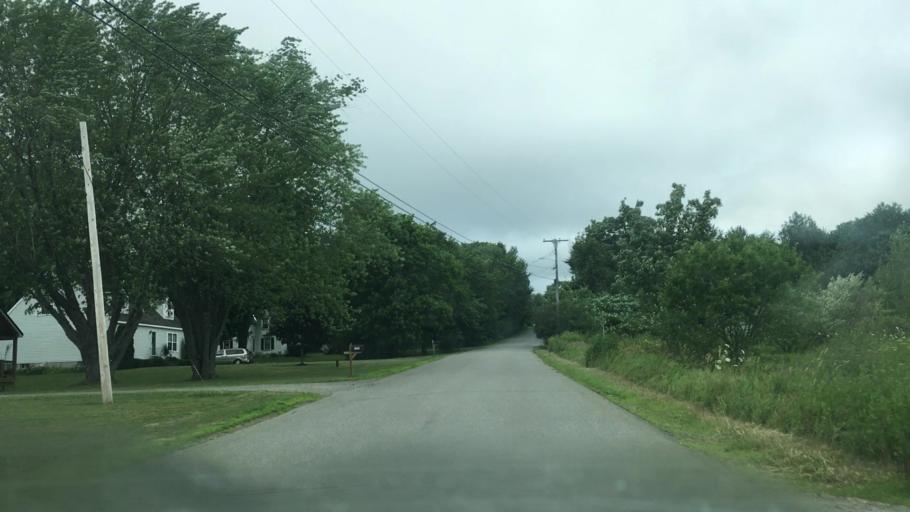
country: US
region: Maine
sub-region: Penobscot County
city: Veazie
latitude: 44.8441
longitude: -68.7461
